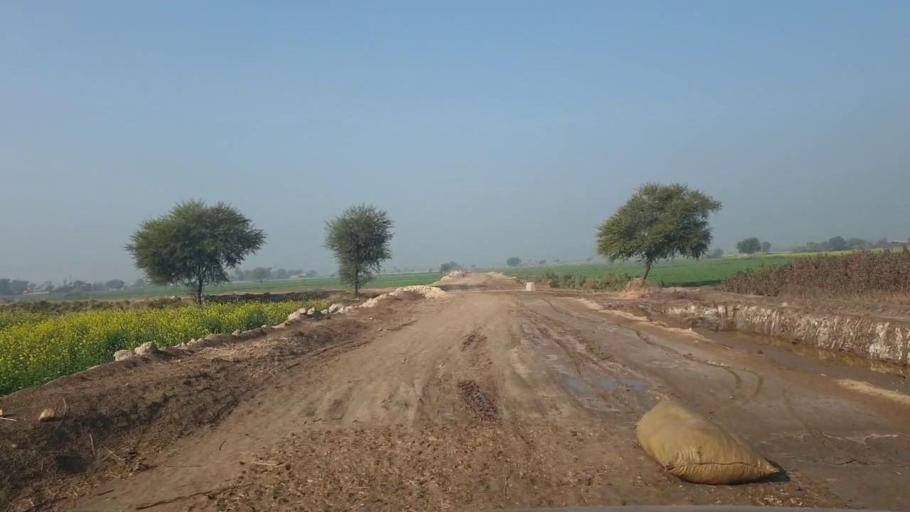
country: PK
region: Sindh
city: Shahdadpur
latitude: 25.9510
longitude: 68.5688
